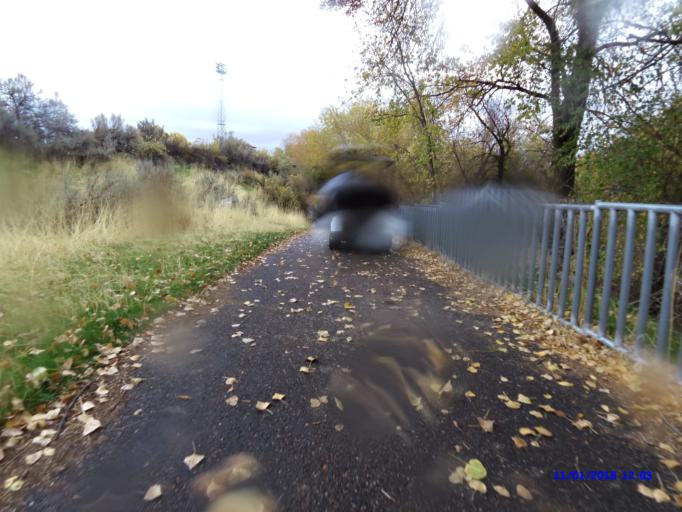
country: US
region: Utah
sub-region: Weber County
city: Ogden
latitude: 41.2288
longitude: -111.9989
